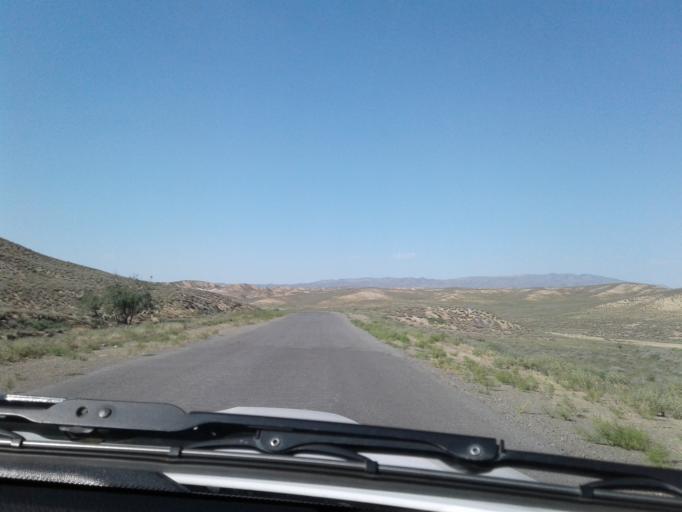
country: TM
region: Balkan
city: Magtymguly
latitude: 38.6597
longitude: 56.2841
